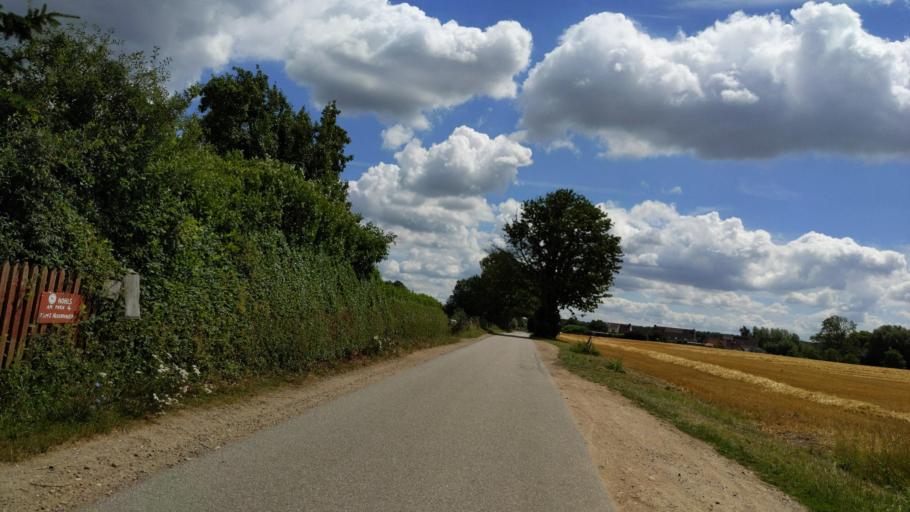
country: DE
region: Mecklenburg-Vorpommern
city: Kalkhorst
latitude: 53.9588
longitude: 11.0162
